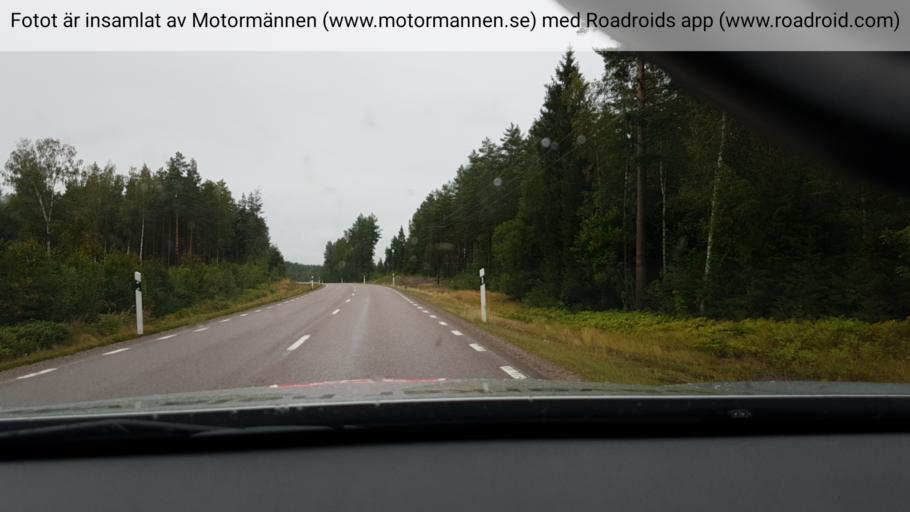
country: SE
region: Gaevleborg
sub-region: Gavle Kommun
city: Hedesunda
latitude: 60.5056
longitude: 16.9404
